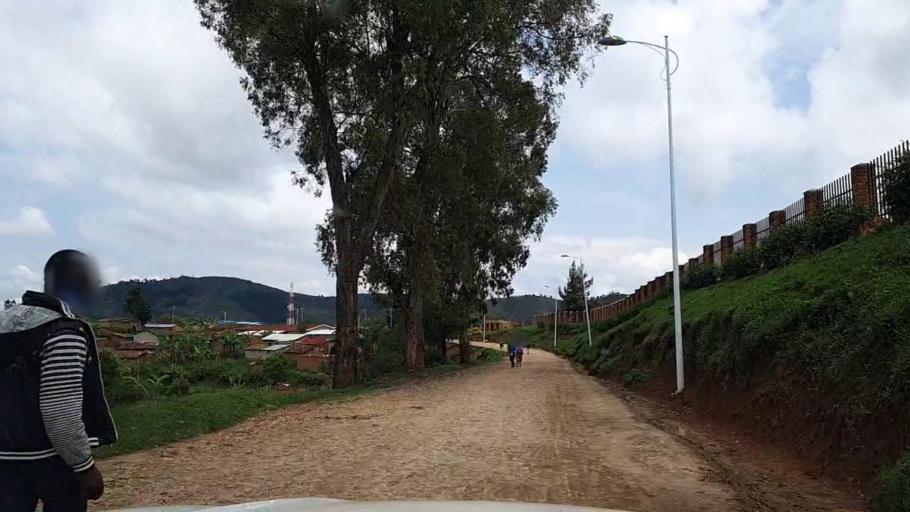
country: RW
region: Southern Province
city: Gikongoro
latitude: -2.3325
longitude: 29.5255
